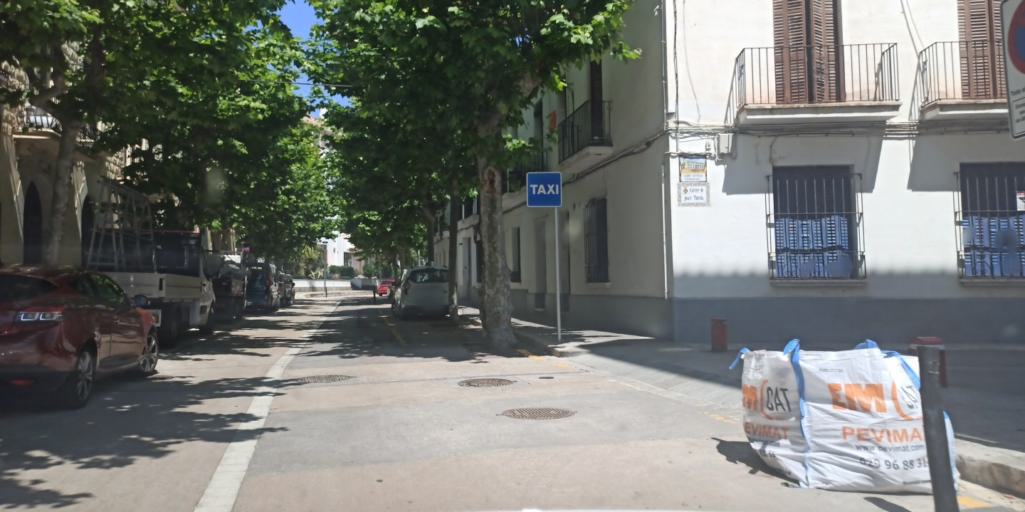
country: ES
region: Catalonia
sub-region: Provincia de Barcelona
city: Sitges
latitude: 41.2353
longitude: 1.8061
